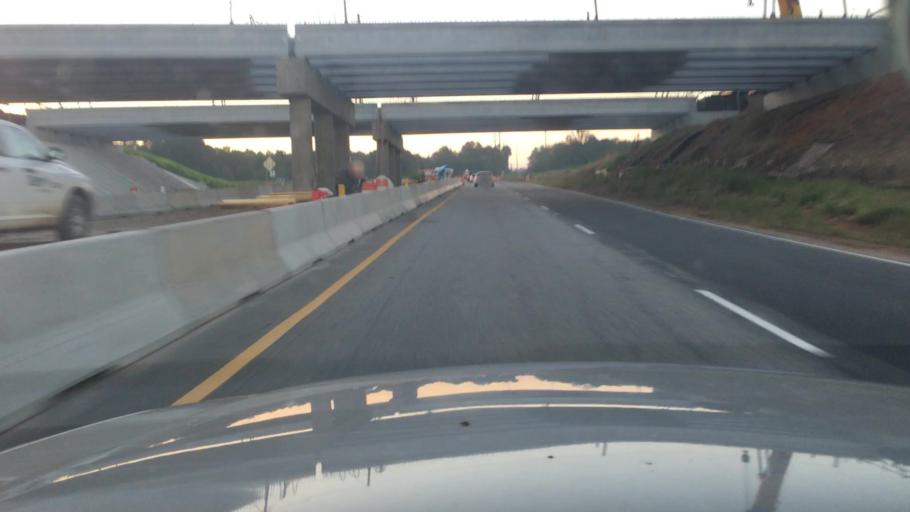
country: US
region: North Carolina
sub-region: Cumberland County
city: Fort Bragg
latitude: 35.0641
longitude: -79.0244
